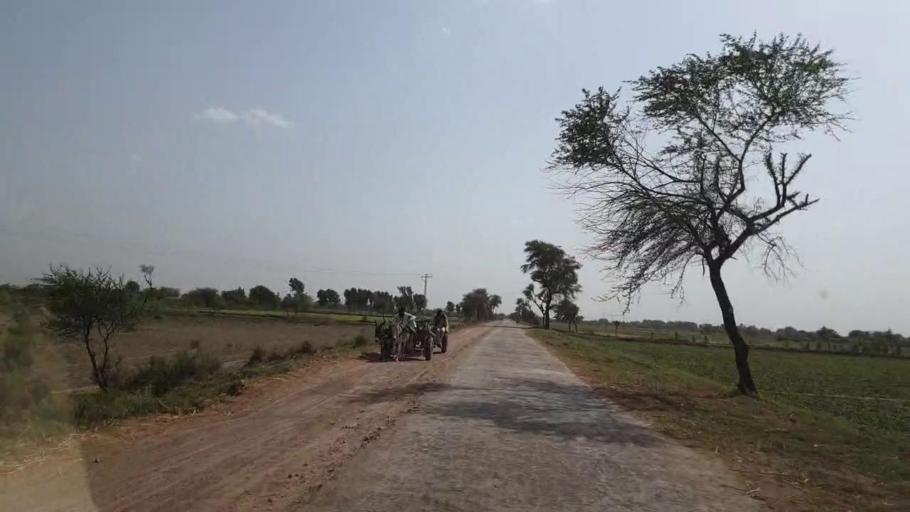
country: PK
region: Sindh
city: Rajo Khanani
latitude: 25.0164
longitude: 68.8728
